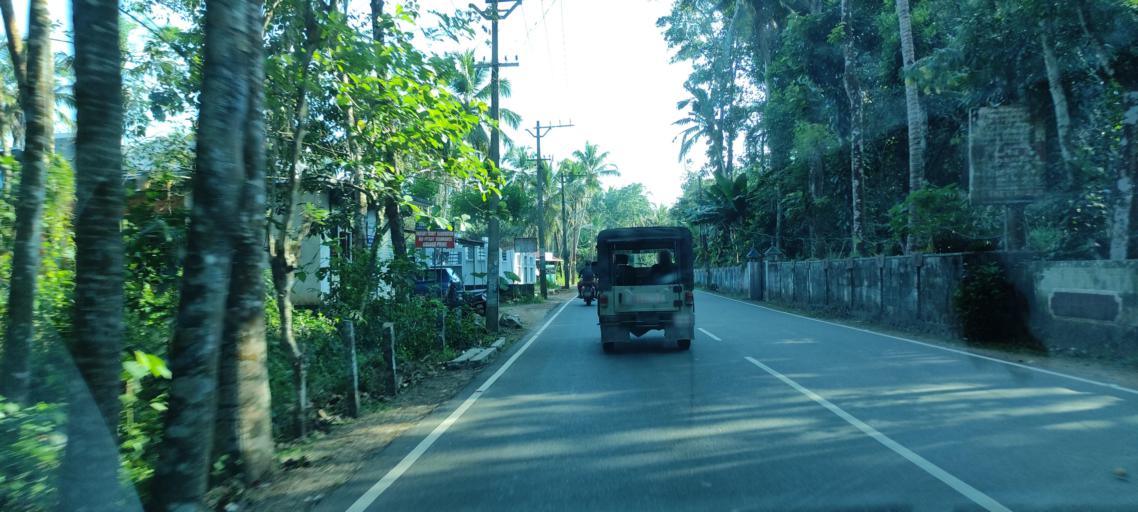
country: IN
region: Kerala
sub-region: Pattanamtitta
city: Adur
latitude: 9.1879
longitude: 76.7447
